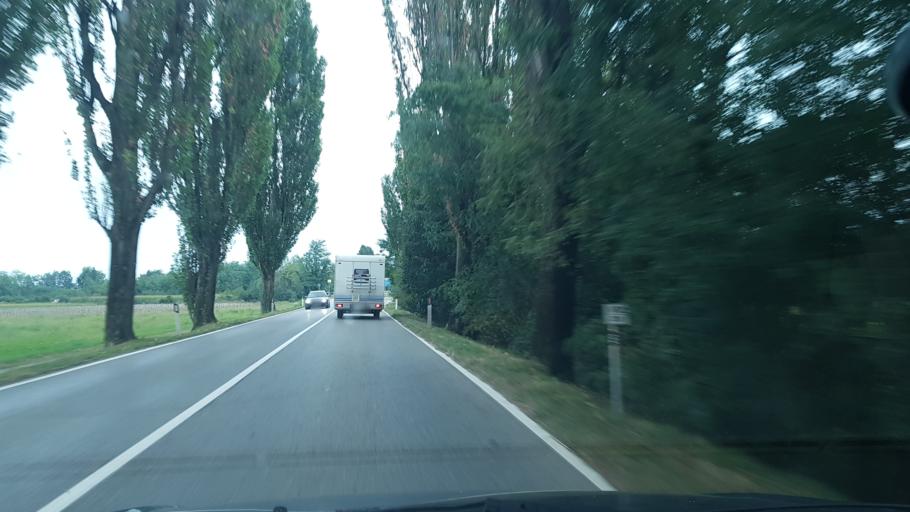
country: IT
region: Friuli Venezia Giulia
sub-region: Provincia di Gorizia
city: Romans d'Isonzo
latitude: 45.8955
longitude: 13.4269
